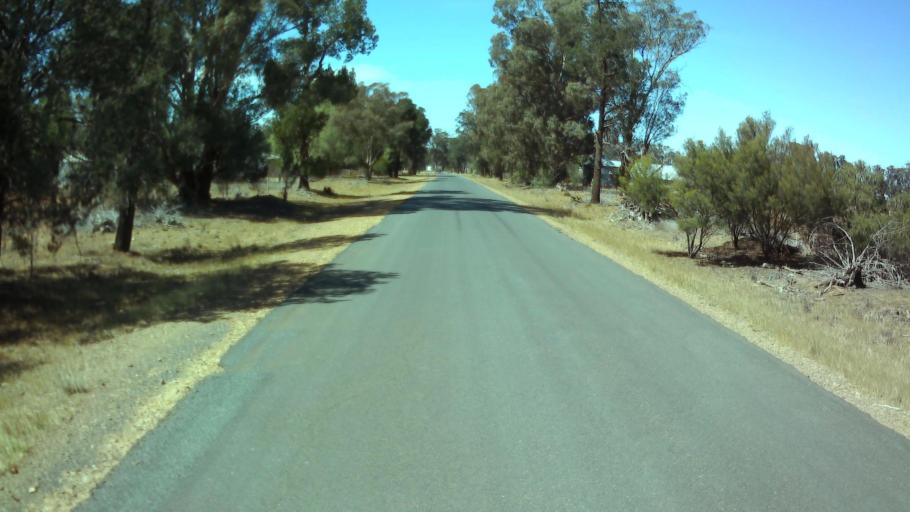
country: AU
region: New South Wales
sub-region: Weddin
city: Grenfell
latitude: -34.1150
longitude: 147.8848
